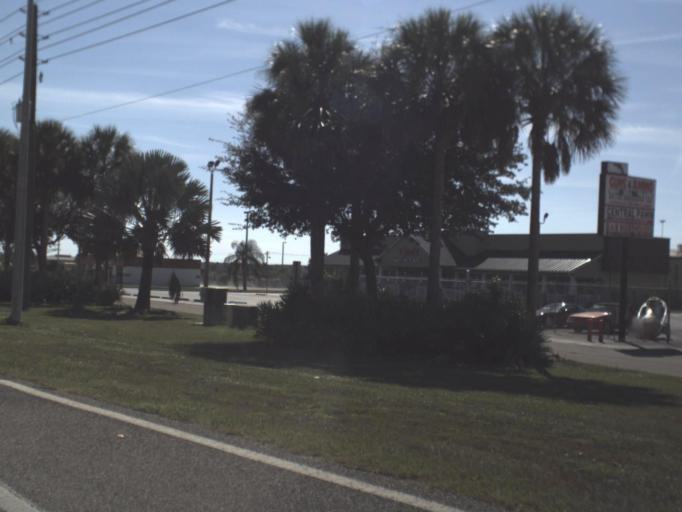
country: US
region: Florida
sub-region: Highlands County
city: Lake Placid
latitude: 27.2904
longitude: -81.3585
